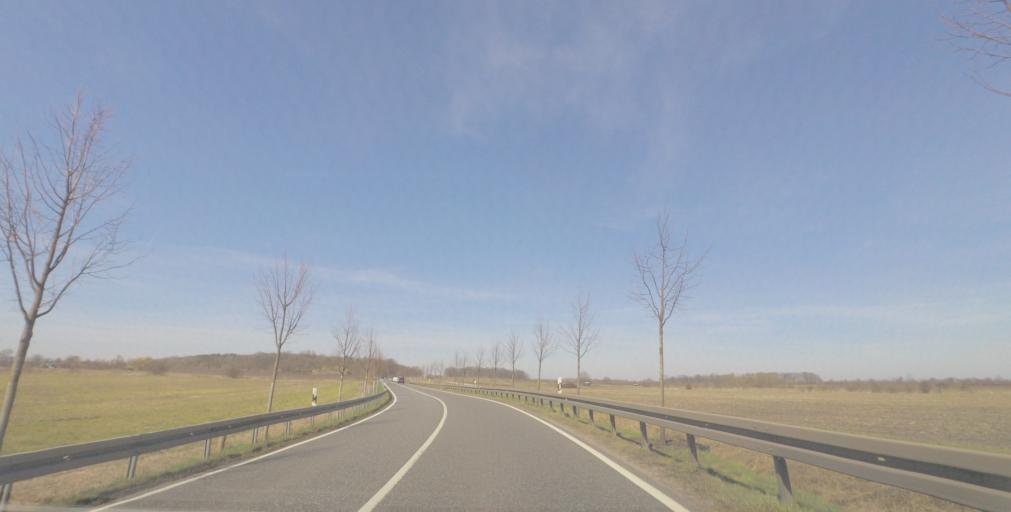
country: DE
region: Brandenburg
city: Potsdam
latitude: 52.4295
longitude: 12.9996
